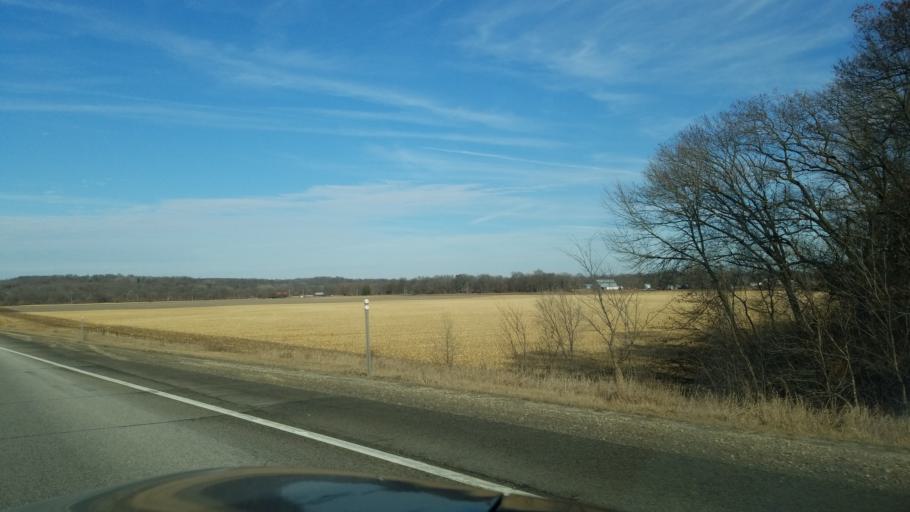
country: US
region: Iowa
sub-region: Linn County
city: Ely
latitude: 41.9308
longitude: -91.5429
